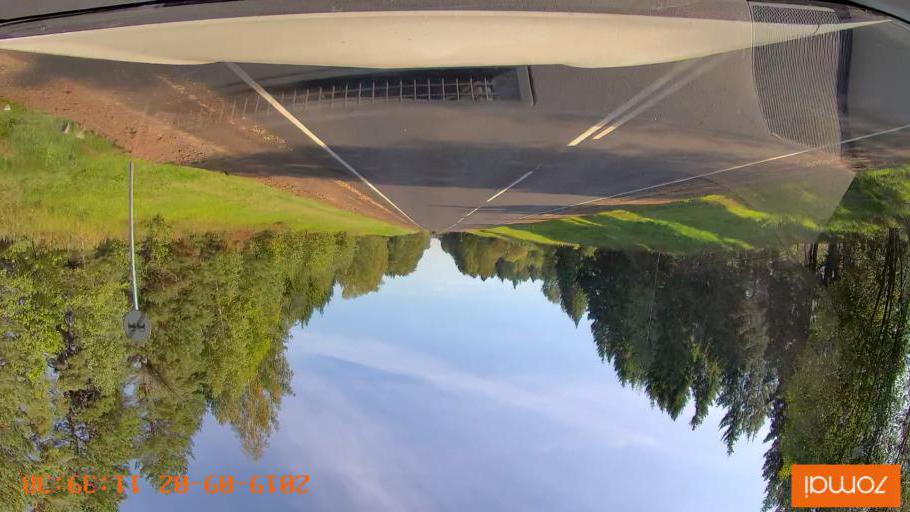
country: RU
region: Smolensk
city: Oster
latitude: 53.9068
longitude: 32.7190
